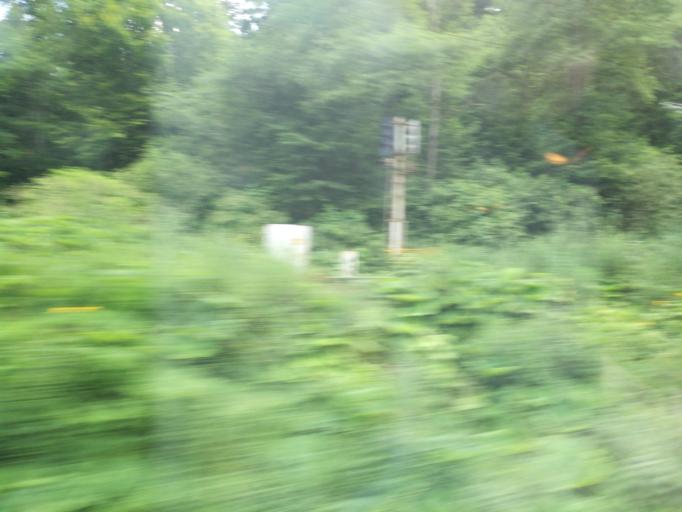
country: RO
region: Brasov
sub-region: Oras Predeal
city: Predeal
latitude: 45.5176
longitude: 25.5962
